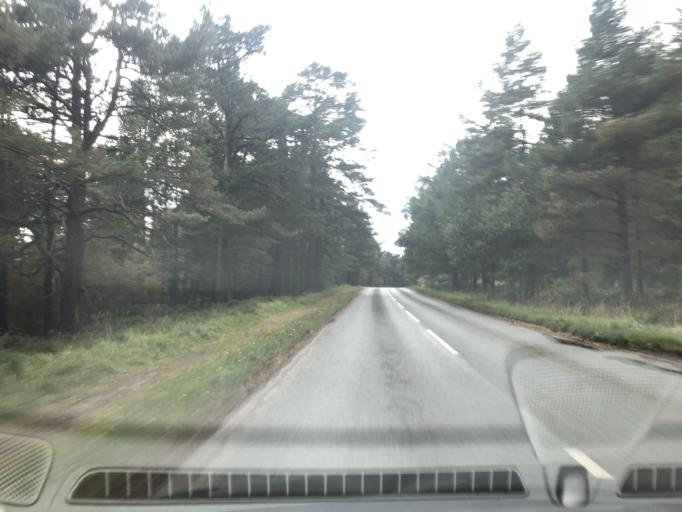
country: GB
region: Scotland
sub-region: Highland
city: Aviemore
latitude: 57.1666
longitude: -3.7192
